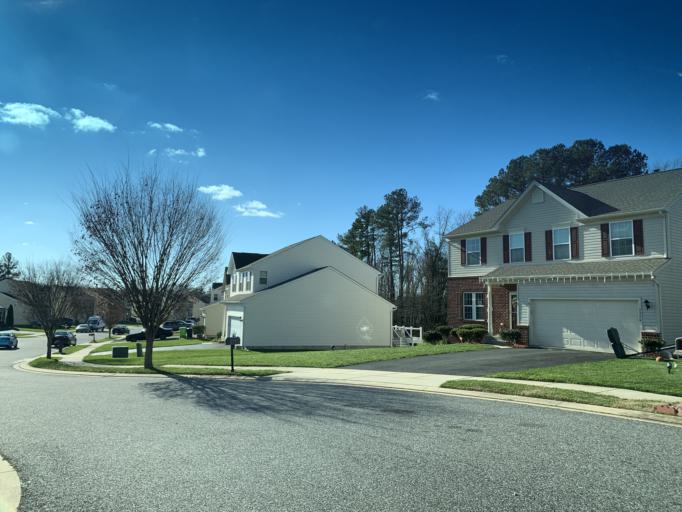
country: US
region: Maryland
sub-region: Harford County
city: Edgewood
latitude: 39.4458
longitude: -76.3047
